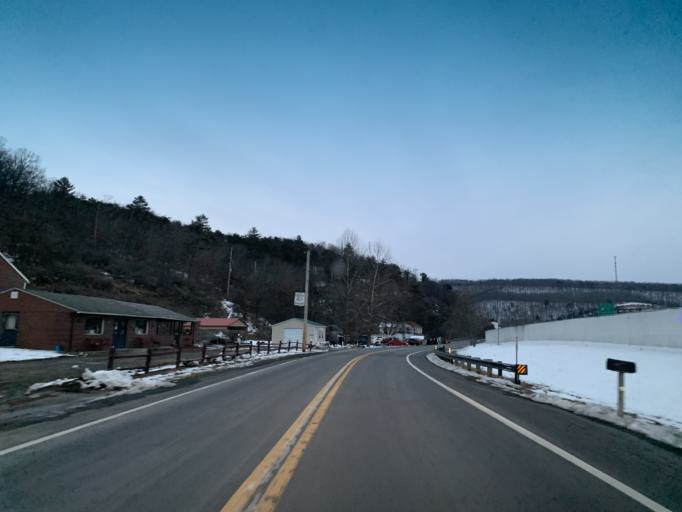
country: US
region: West Virginia
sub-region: Morgan County
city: Berkeley Springs
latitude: 39.6784
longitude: -78.4658
